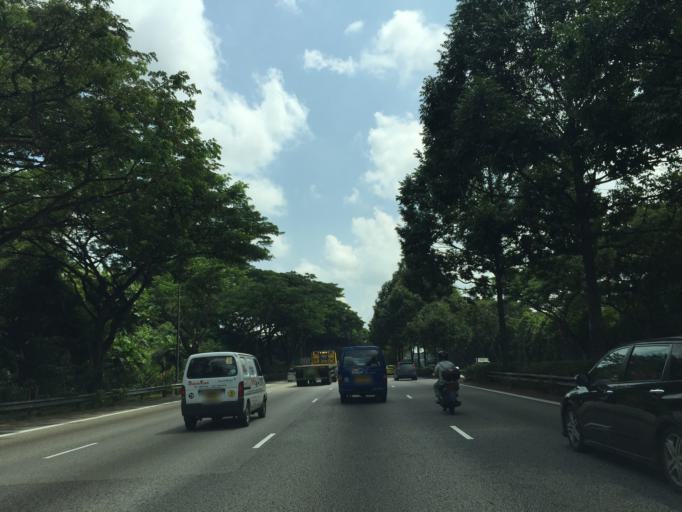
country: SG
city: Singapore
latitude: 1.3295
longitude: 103.8223
